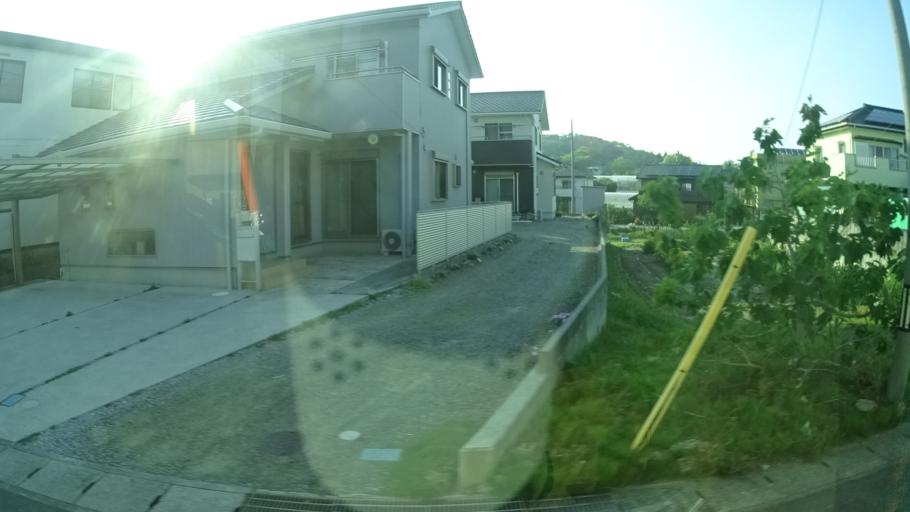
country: JP
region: Aichi
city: Tahara
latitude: 34.6636
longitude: 137.2578
